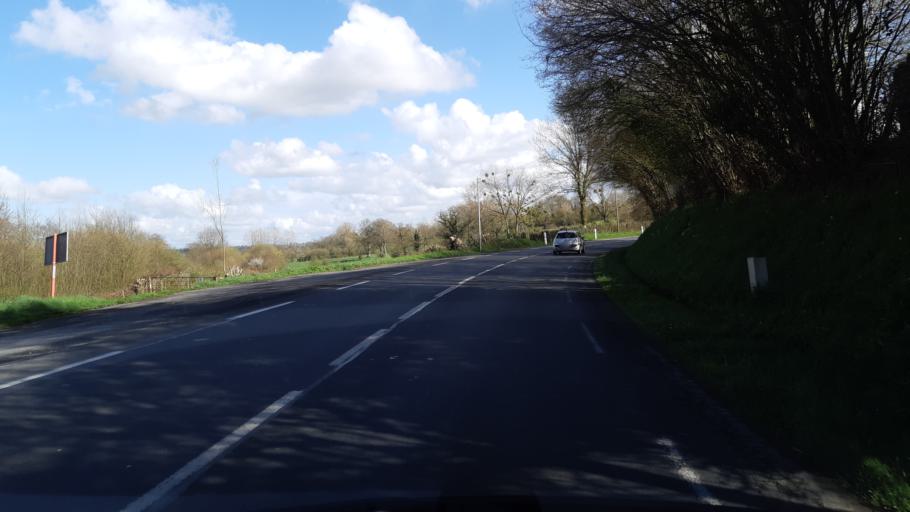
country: FR
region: Lower Normandy
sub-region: Departement de la Manche
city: Agneaux
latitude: 49.0882
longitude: -1.1157
